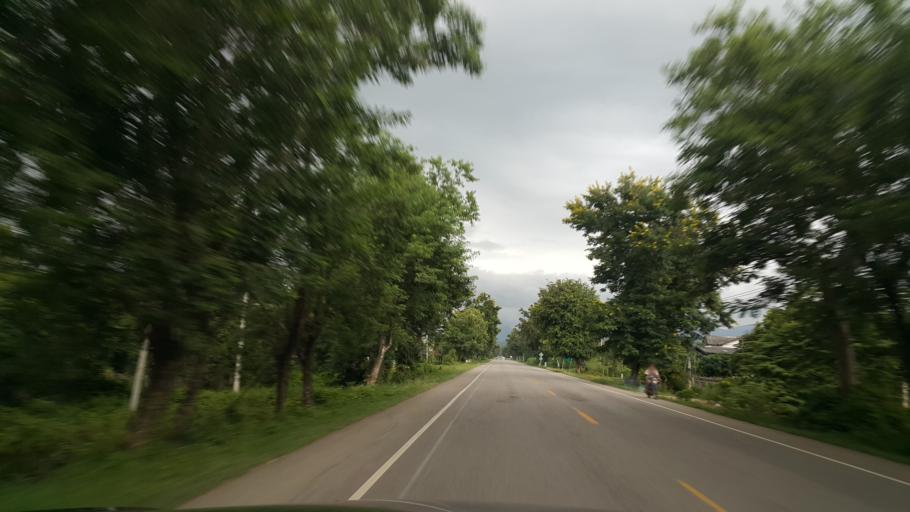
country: TH
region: Phayao
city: Dok Kham Tai
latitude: 19.2062
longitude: 100.0349
